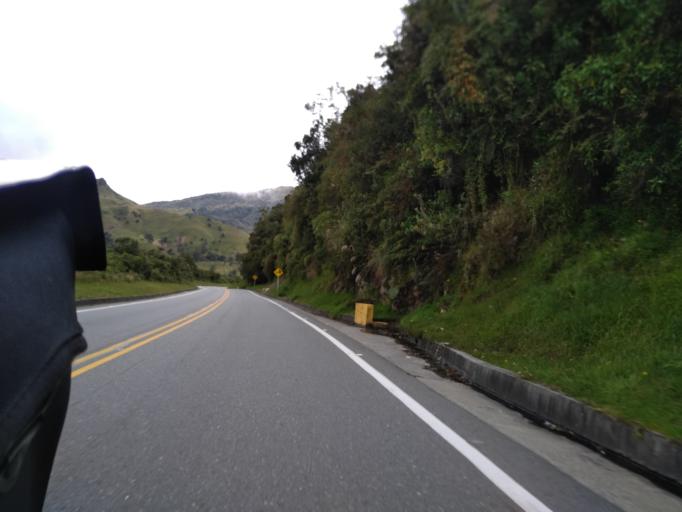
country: CO
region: Tolima
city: Herveo
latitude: 5.0226
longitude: -75.3339
